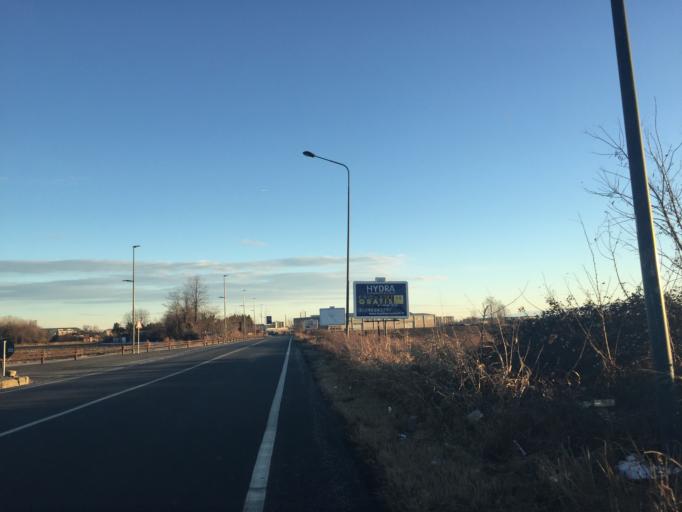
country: IT
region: Piedmont
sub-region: Provincia di Torino
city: Gerbido
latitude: 45.0508
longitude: 7.6015
